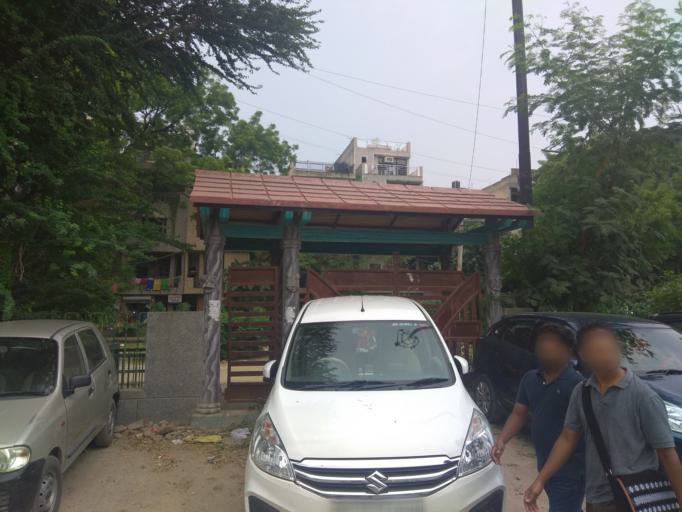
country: IN
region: NCT
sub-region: New Delhi
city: New Delhi
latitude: 28.5718
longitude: 77.2540
